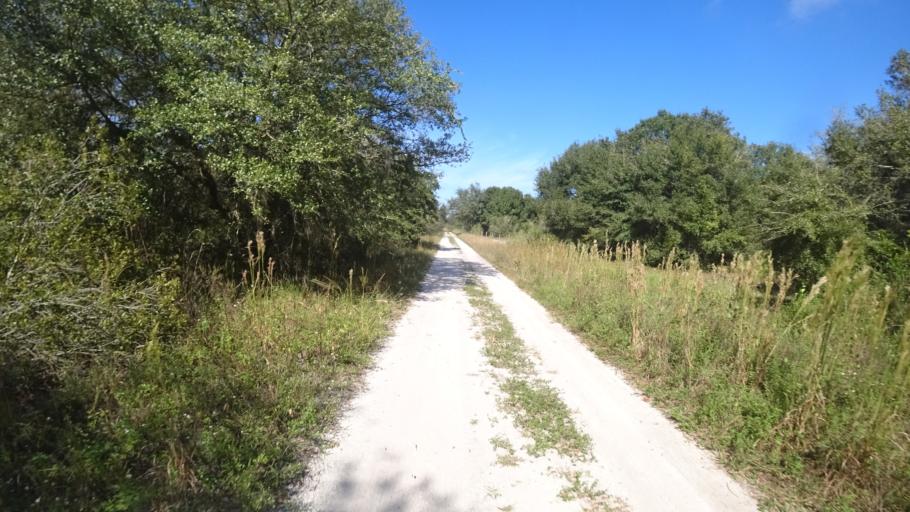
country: US
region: Florida
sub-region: DeSoto County
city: Arcadia
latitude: 27.2918
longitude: -82.0643
